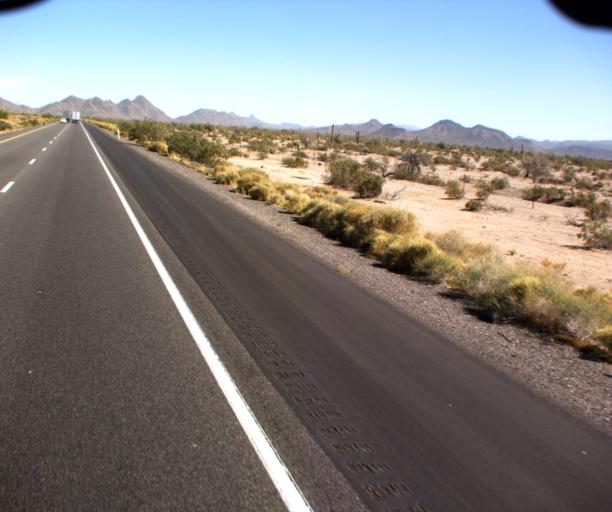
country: US
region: Arizona
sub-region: Maricopa County
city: Gila Bend
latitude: 32.9094
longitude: -112.5994
